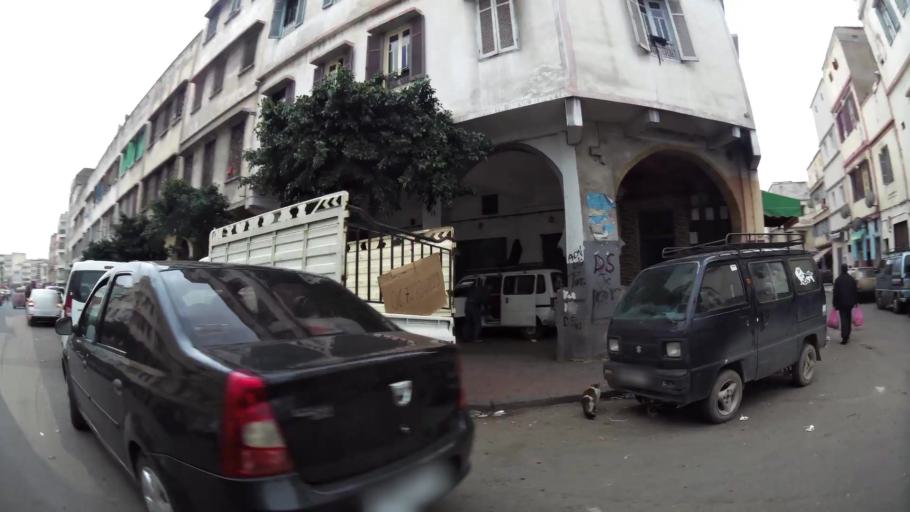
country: MA
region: Grand Casablanca
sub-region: Casablanca
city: Casablanca
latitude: 33.5698
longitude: -7.6051
